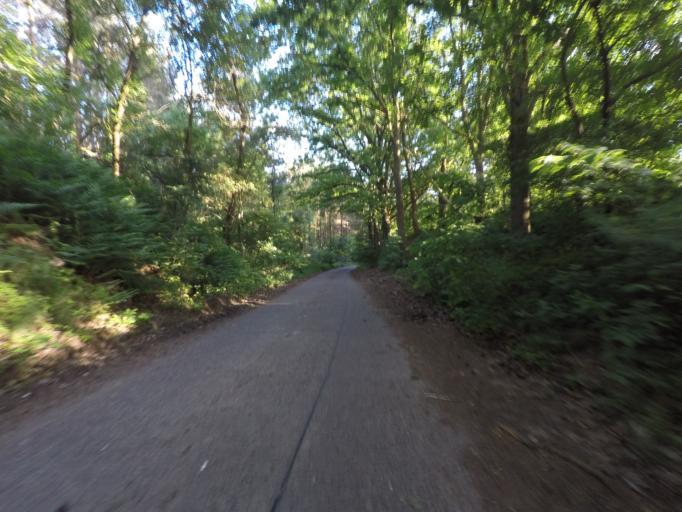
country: DE
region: Brandenburg
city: Melchow
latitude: 52.8627
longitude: 13.6881
